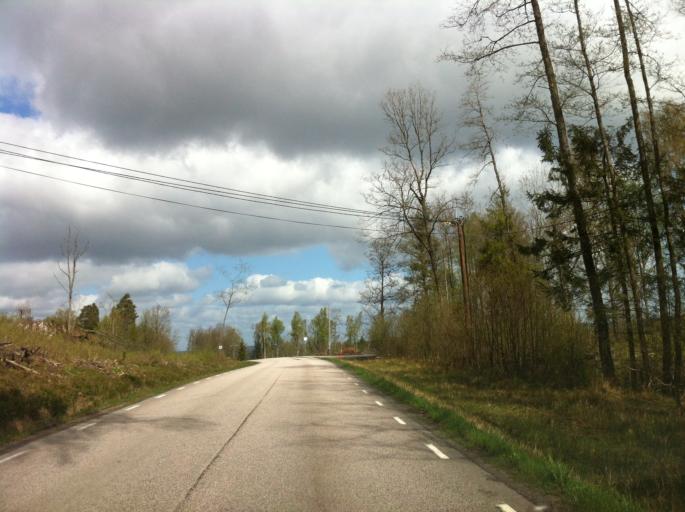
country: SE
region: Vaestra Goetaland
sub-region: Alingsas Kommun
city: Alingsas
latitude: 57.8506
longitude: 12.5593
